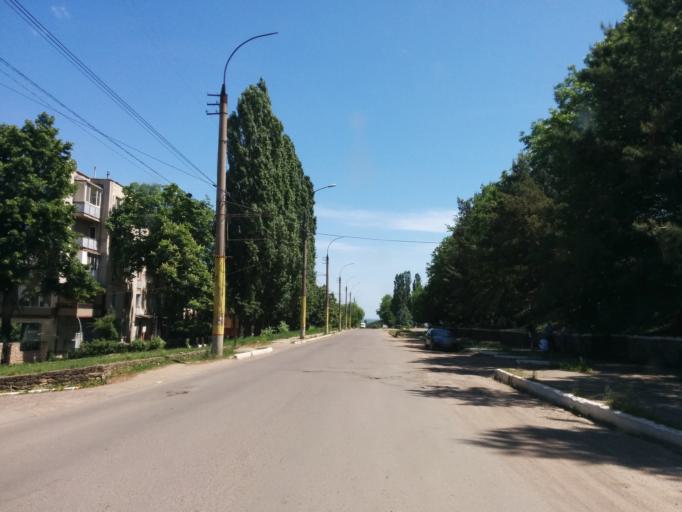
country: MD
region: Raionul Soroca
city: Soroca
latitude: 48.1626
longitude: 28.2702
